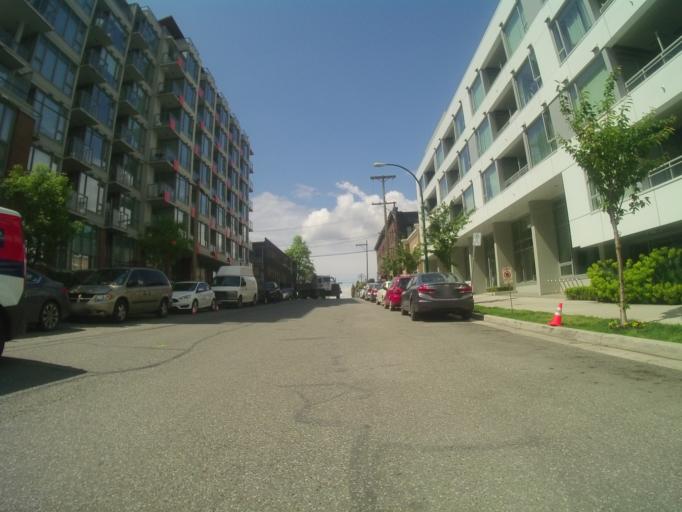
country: CA
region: British Columbia
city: Vancouver
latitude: 49.2655
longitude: -123.0992
